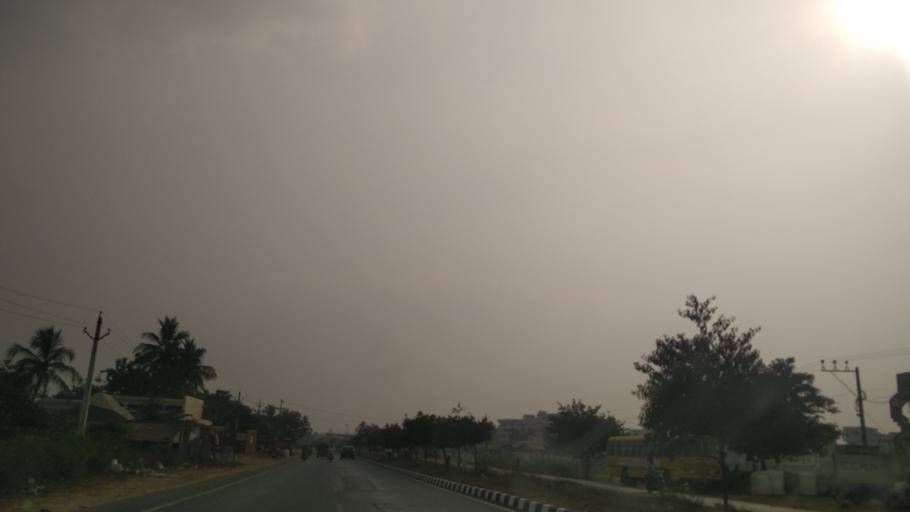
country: IN
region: Andhra Pradesh
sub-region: East Godavari
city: Rajahmundry
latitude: 16.9878
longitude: 81.7992
